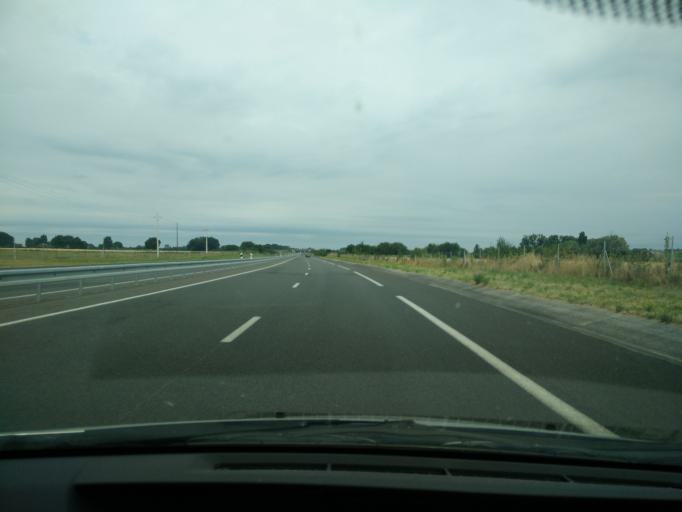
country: FR
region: Pays de la Loire
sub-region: Departement de Maine-et-Loire
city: Saint-Jean
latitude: 47.2744
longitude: -0.3388
